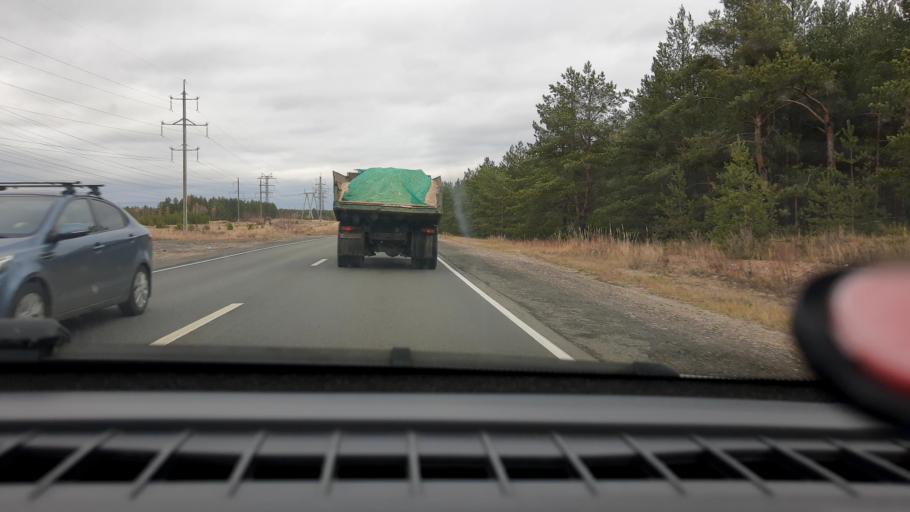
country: RU
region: Nizjnij Novgorod
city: Lukino
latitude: 56.3810
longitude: 43.6312
